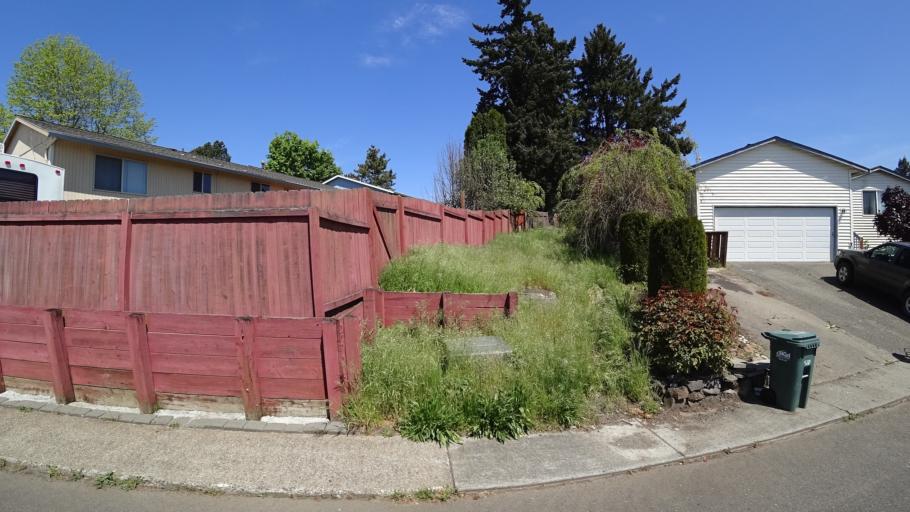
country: US
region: Oregon
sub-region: Washington County
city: Hillsboro
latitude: 45.5050
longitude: -122.9700
